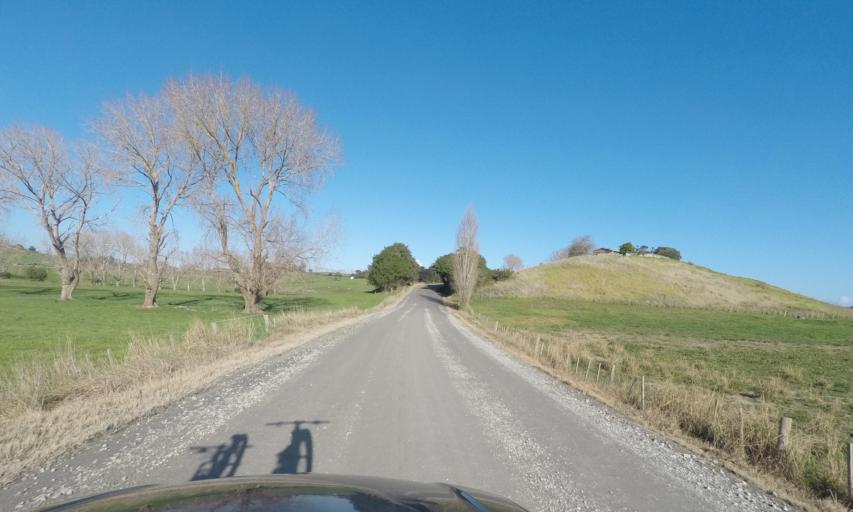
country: NZ
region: Auckland
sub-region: Auckland
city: Wellsford
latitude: -36.1514
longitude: 174.6059
